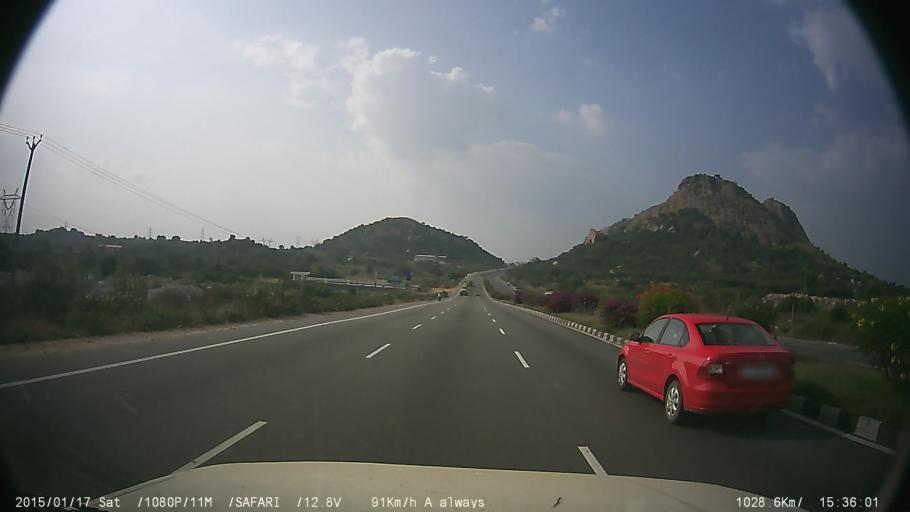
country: IN
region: Tamil Nadu
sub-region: Krishnagiri
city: Kelamangalam
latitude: 12.6534
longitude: 78.0273
